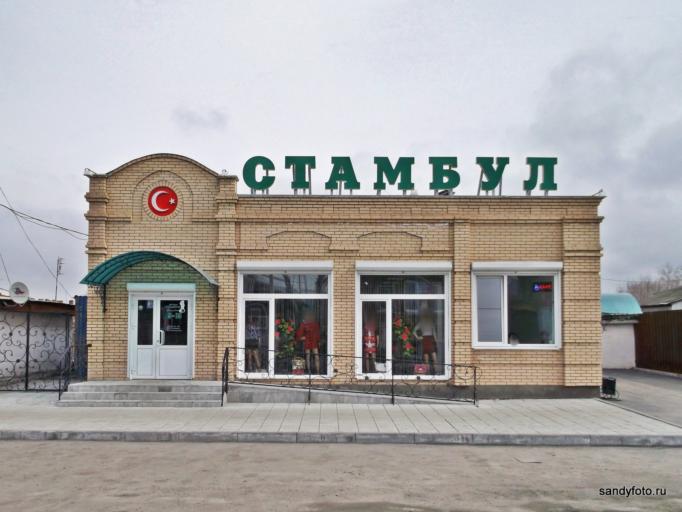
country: RU
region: Chelyabinsk
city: Troitsk
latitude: 54.0858
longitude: 61.5664
